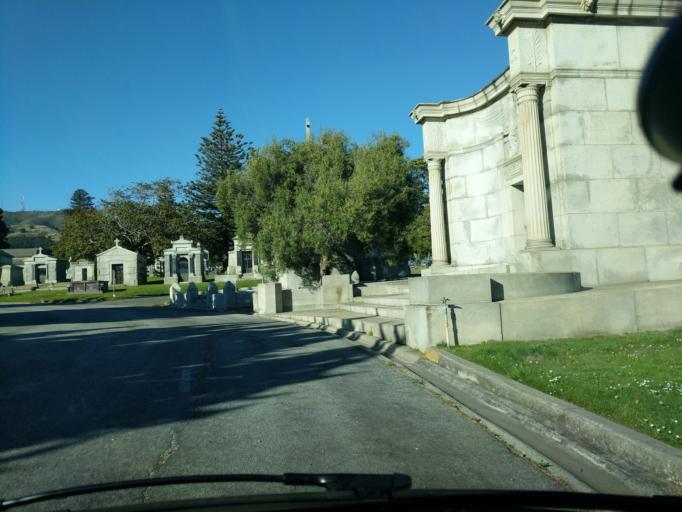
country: US
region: California
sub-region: San Mateo County
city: Colma
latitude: 37.6697
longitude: -122.4467
